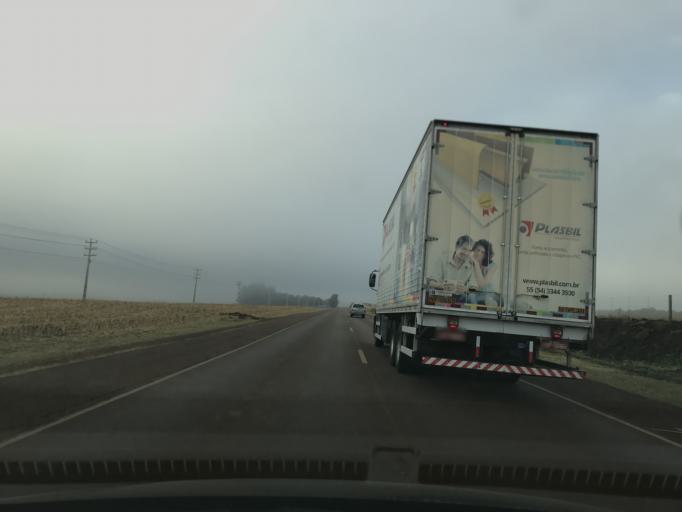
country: BR
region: Parana
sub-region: Toledo
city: Toledo
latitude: -24.6751
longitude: -53.6967
